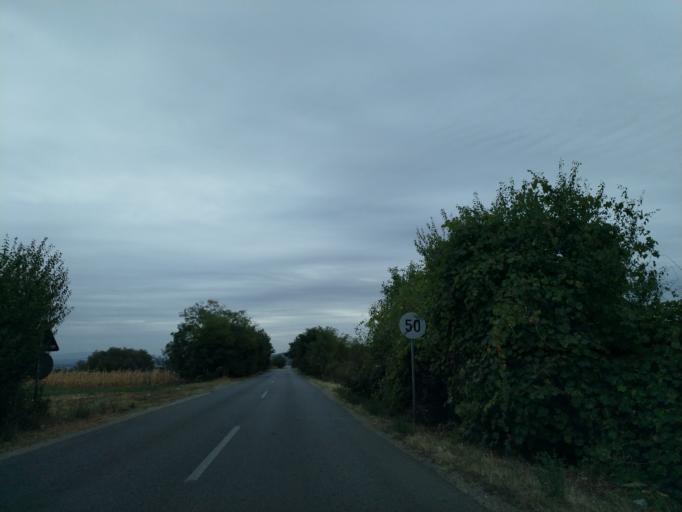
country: RS
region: Central Serbia
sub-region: Pomoravski Okrug
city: Jagodina
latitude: 44.0063
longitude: 21.2068
